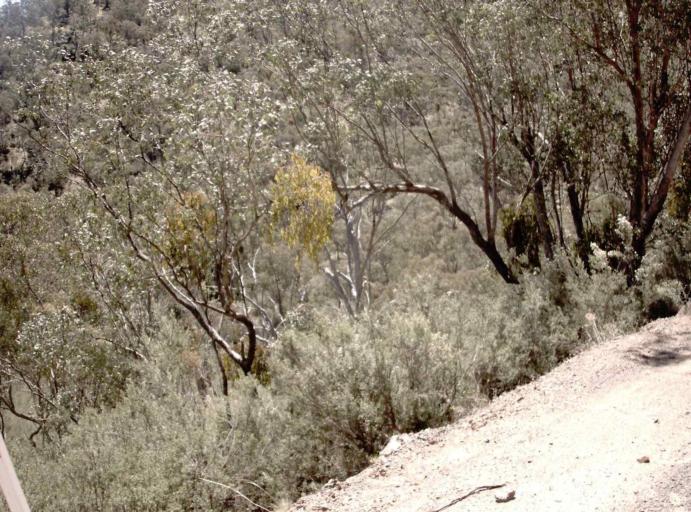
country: AU
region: New South Wales
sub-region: Snowy River
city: Jindabyne
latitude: -37.0421
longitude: 148.5378
